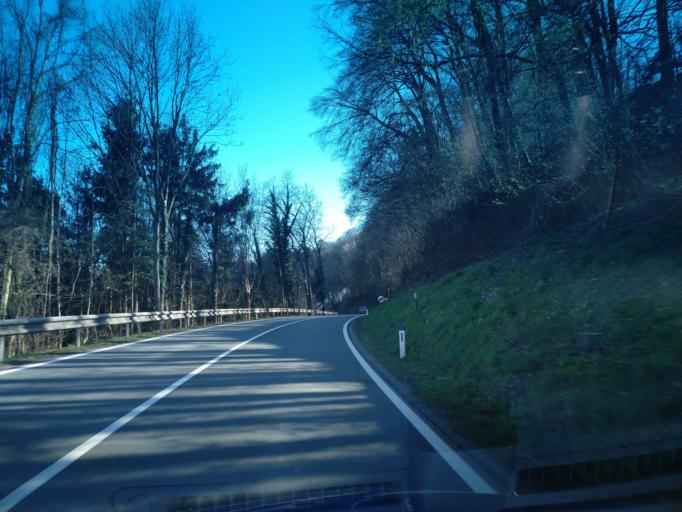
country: AT
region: Styria
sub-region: Politischer Bezirk Leibnitz
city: Stocking
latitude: 46.8776
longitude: 15.5273
